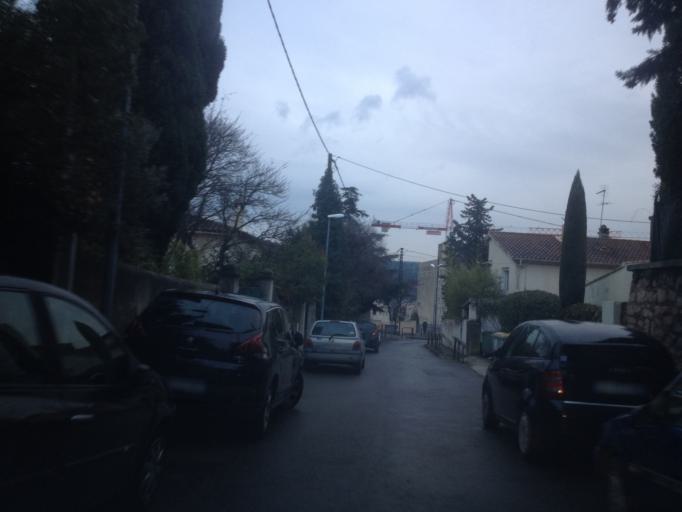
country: FR
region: Provence-Alpes-Cote d'Azur
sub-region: Departement des Bouches-du-Rhone
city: Aix-en-Provence
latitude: 43.5157
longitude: 5.4487
